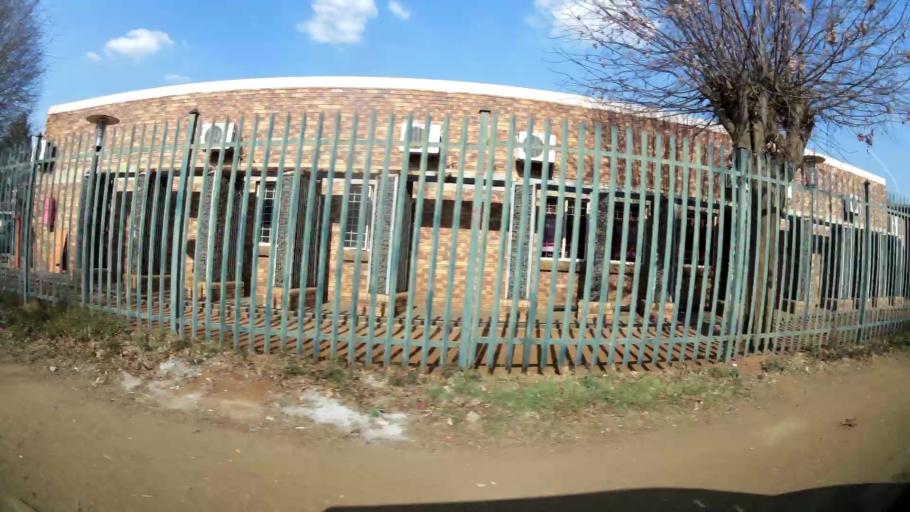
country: ZA
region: Gauteng
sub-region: Ekurhuleni Metropolitan Municipality
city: Brakpan
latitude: -26.1529
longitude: 28.4149
